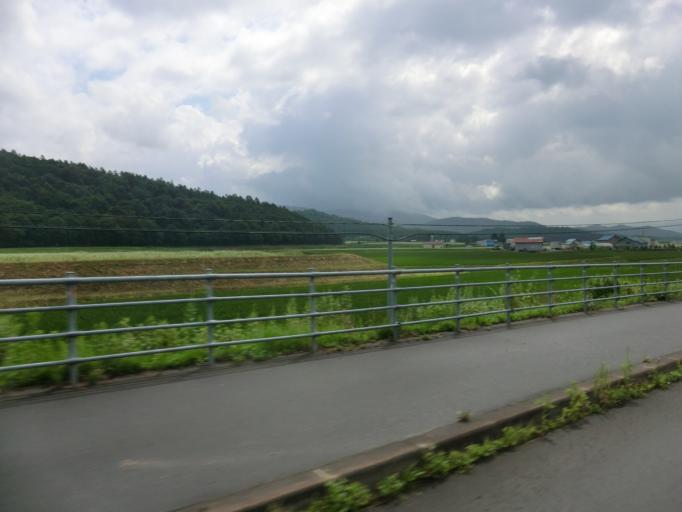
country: JP
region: Hokkaido
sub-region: Asahikawa-shi
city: Asahikawa
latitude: 44.0469
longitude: 142.1473
